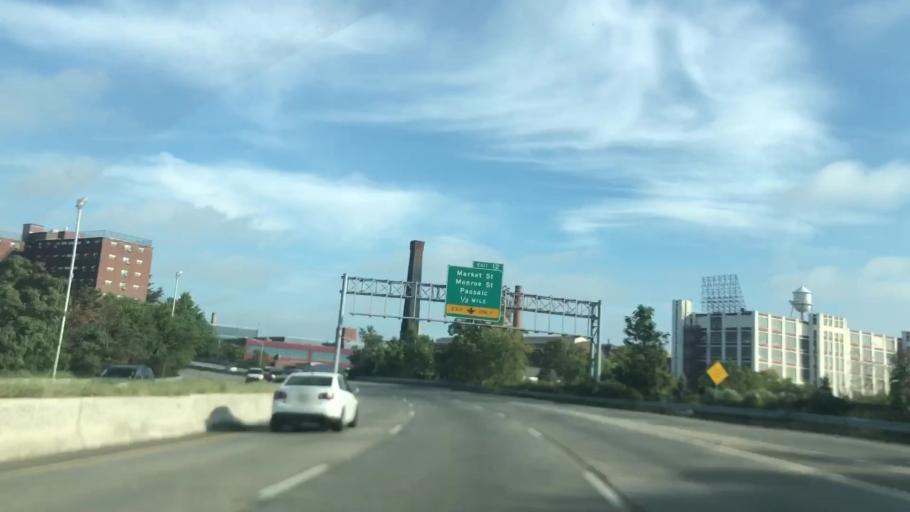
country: US
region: New Jersey
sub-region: Bergen County
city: Wallington
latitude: 40.8583
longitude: -74.1203
